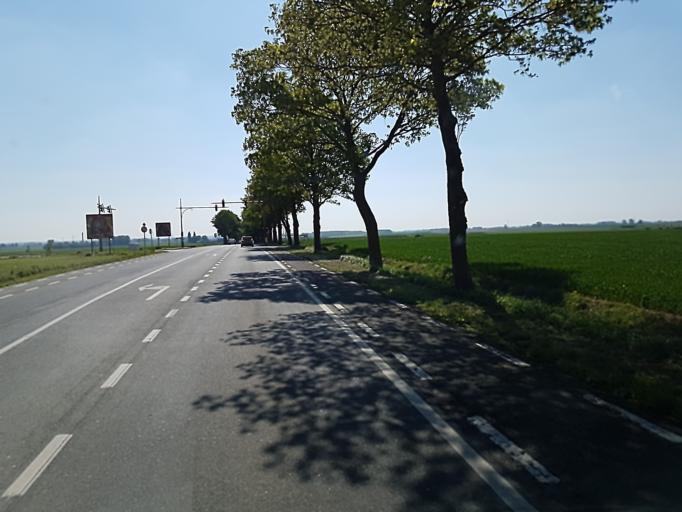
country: BE
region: Wallonia
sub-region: Province du Hainaut
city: Brugelette
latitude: 50.5737
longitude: 3.8709
